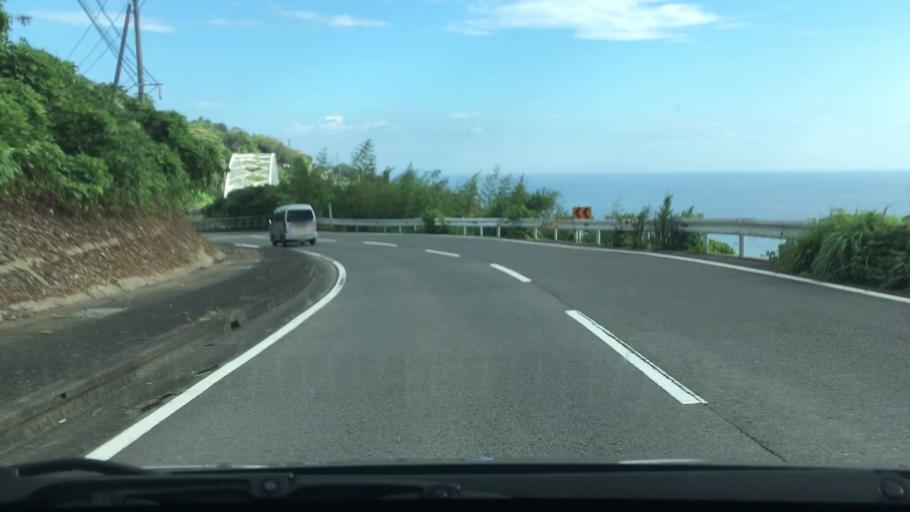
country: JP
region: Nagasaki
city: Togitsu
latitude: 32.8597
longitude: 129.6850
